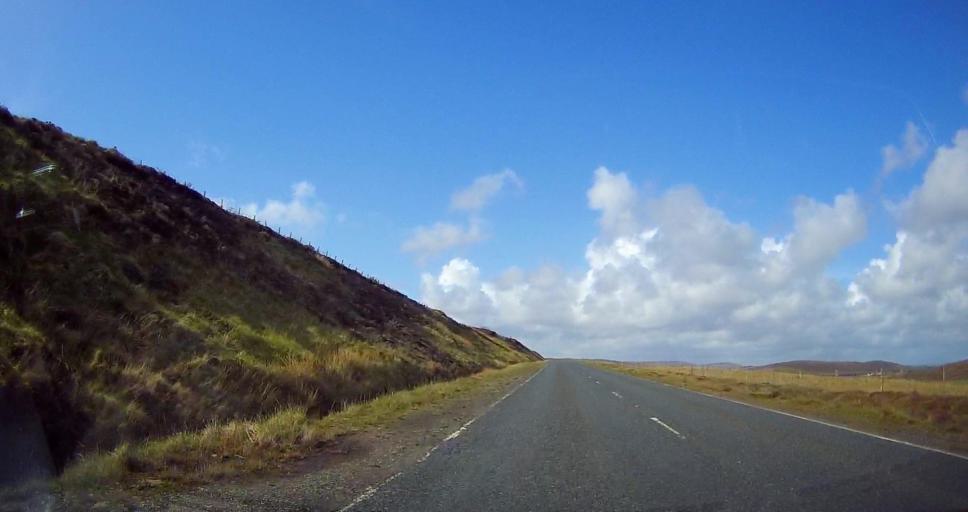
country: GB
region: Scotland
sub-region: Shetland Islands
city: Lerwick
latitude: 60.2153
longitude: -1.2339
